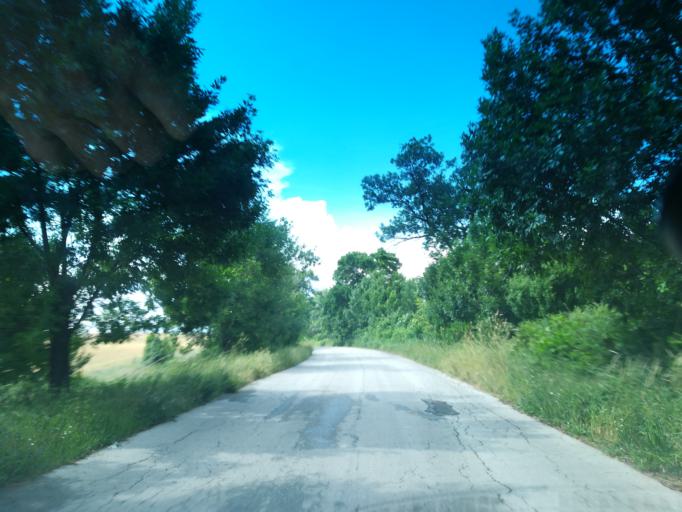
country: BG
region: Khaskovo
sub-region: Obshtina Mineralni Bani
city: Mineralni Bani
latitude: 41.9999
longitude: 25.2250
